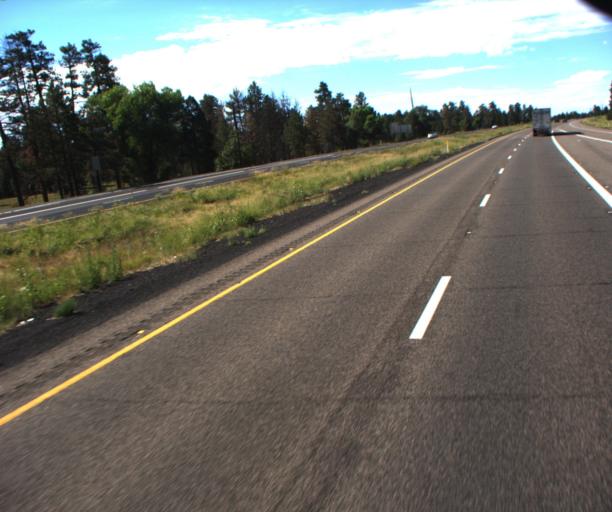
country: US
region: Arizona
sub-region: Coconino County
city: Sedona
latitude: 34.9105
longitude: -111.6413
